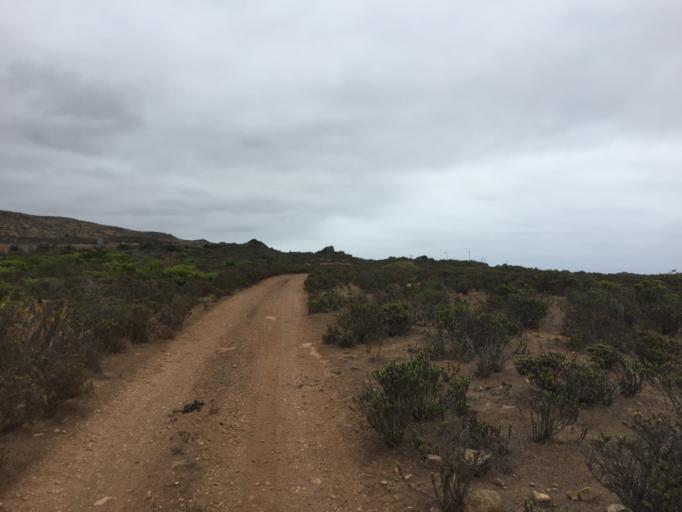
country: CL
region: Valparaiso
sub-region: Petorca Province
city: La Ligua
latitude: -32.1663
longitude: -71.5199
